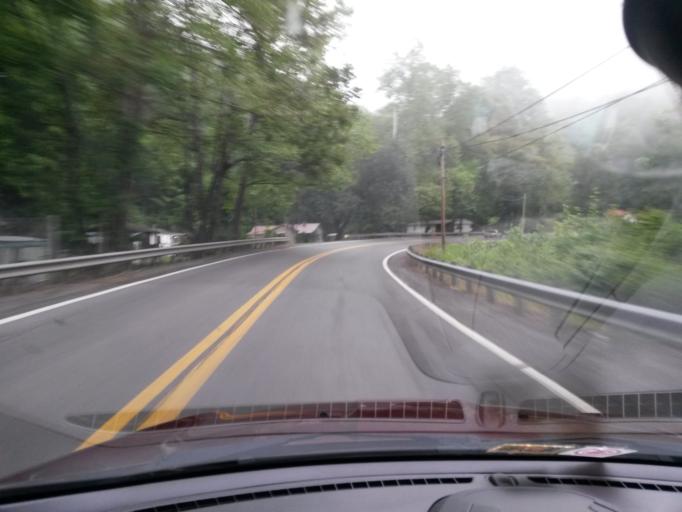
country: US
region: West Virginia
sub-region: McDowell County
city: Welch
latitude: 37.5053
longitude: -81.5615
